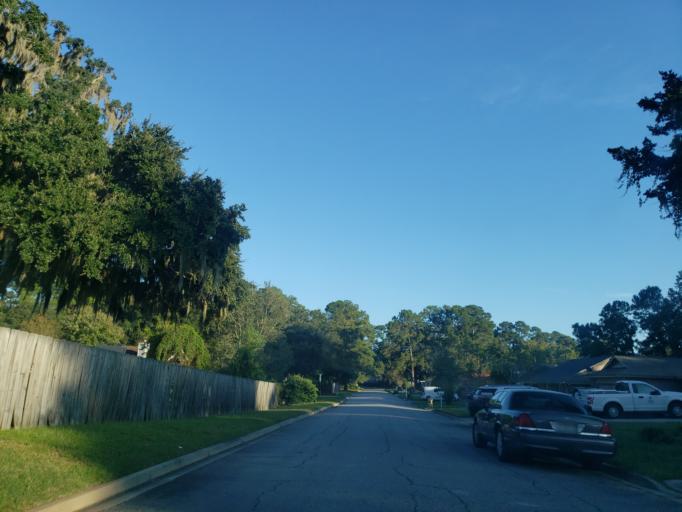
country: US
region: Georgia
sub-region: Chatham County
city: Isle of Hope
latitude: 31.9965
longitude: -81.0654
